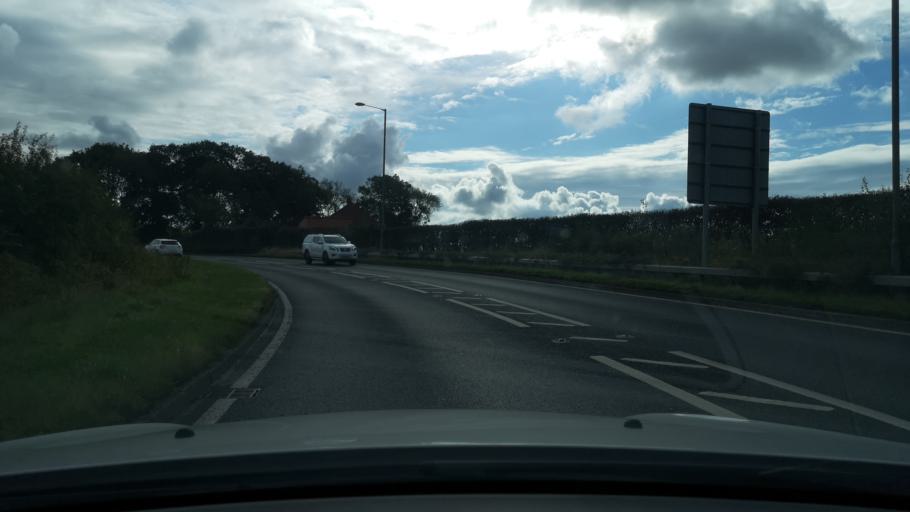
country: GB
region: England
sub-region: East Riding of Yorkshire
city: Cherry Burton
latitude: 53.8591
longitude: -0.4795
